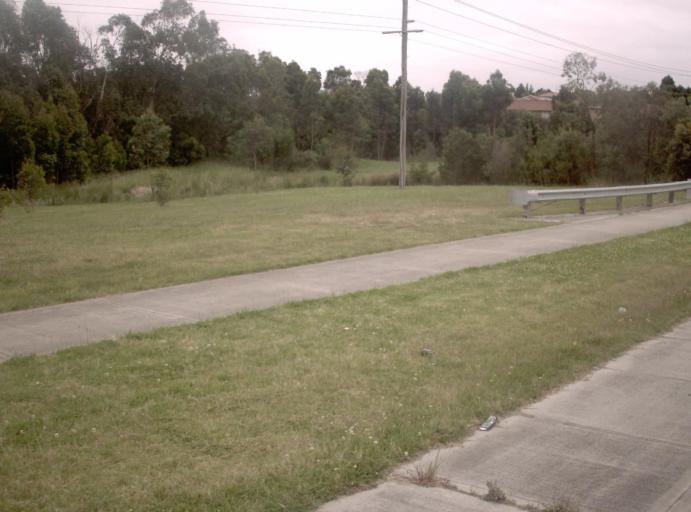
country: AU
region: Victoria
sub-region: Casey
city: Endeavour Hills
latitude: -37.9885
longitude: 145.2766
